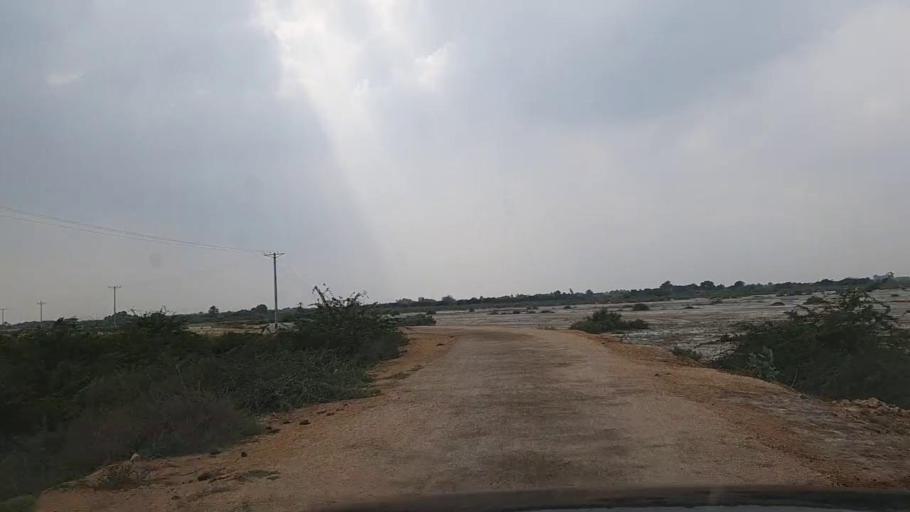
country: PK
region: Sindh
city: Thatta
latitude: 24.8262
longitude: 67.8220
